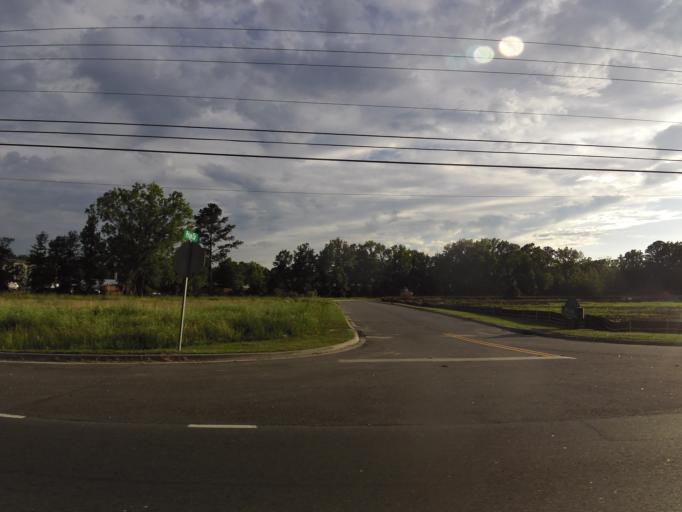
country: US
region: Georgia
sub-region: Chatham County
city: Pooler
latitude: 32.1018
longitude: -81.2236
